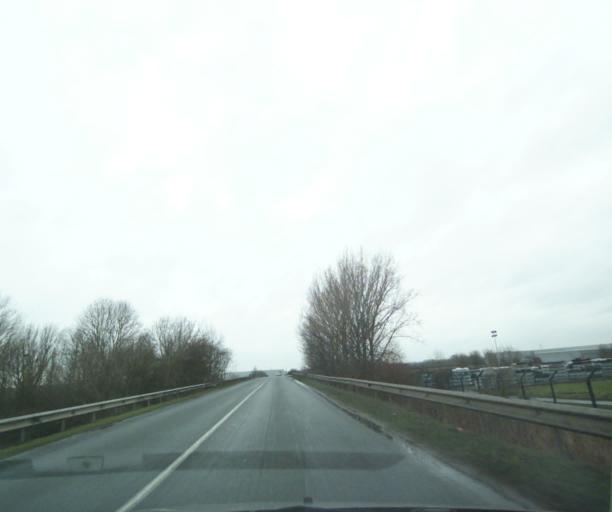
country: FR
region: Nord-Pas-de-Calais
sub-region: Departement du Nord
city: Prouvy
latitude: 50.3326
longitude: 3.4468
